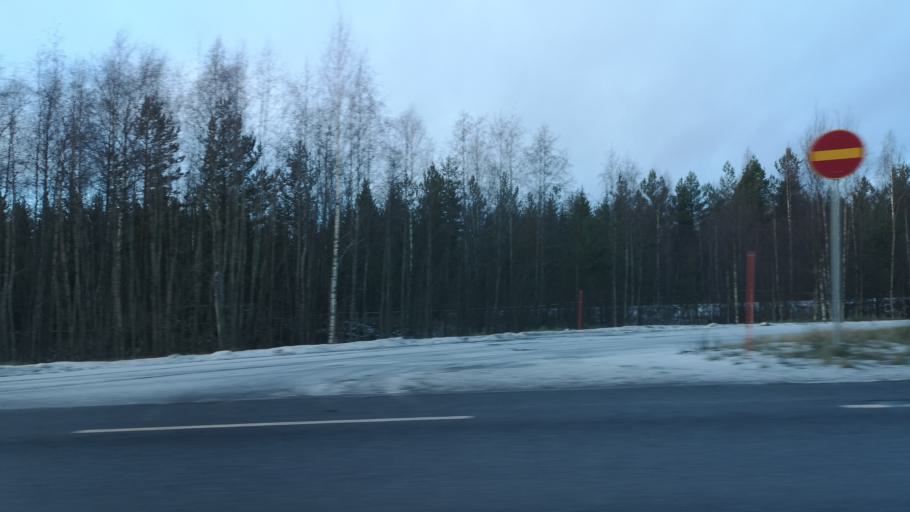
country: FI
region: Southern Savonia
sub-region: Mikkeli
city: Pertunmaa
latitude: 61.3808
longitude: 26.3051
